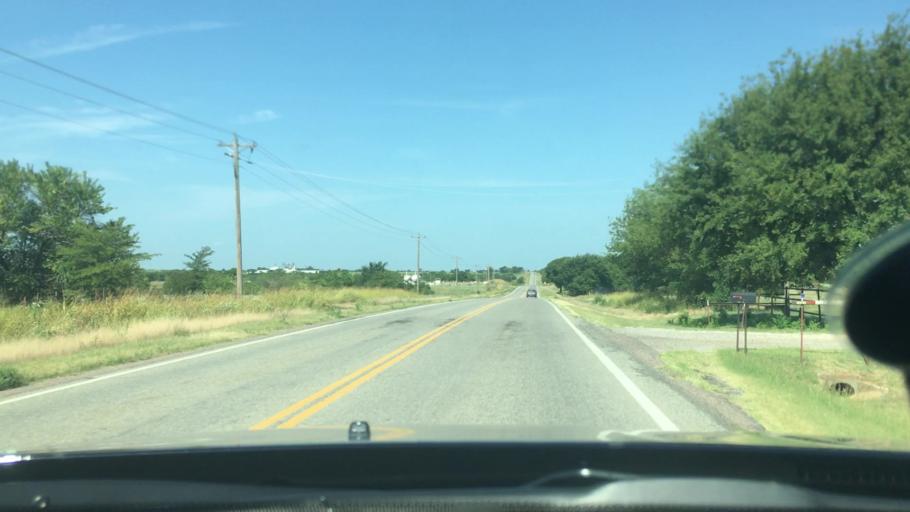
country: US
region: Oklahoma
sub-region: Marshall County
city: Kingston
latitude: 33.9982
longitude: -96.7737
